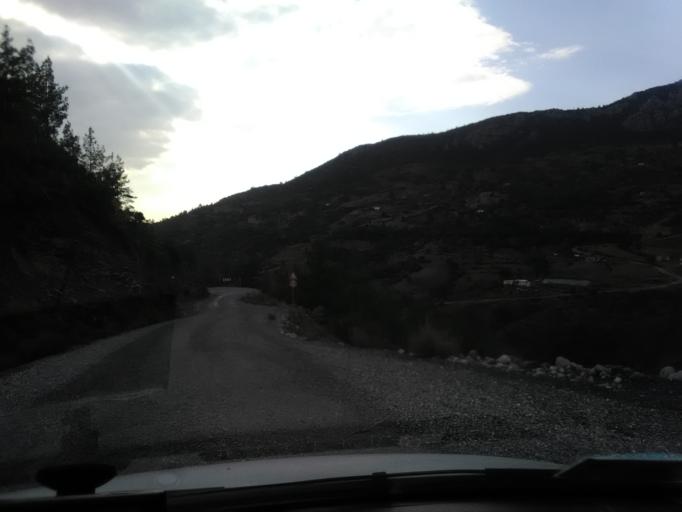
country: TR
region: Antalya
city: Gazipasa
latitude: 36.3038
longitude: 32.3831
